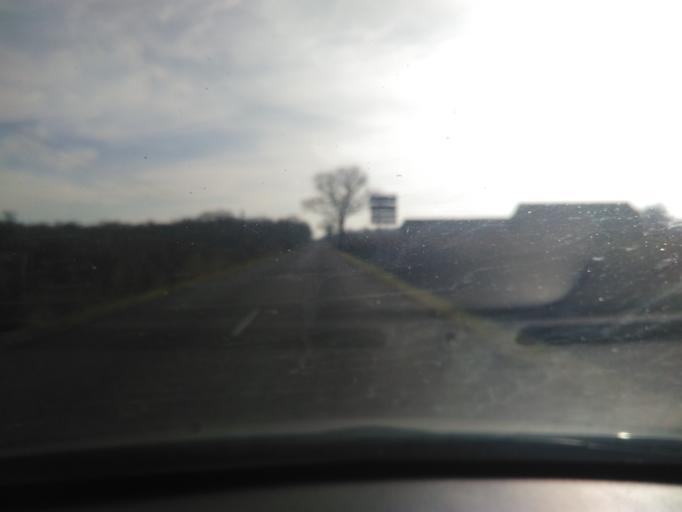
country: FR
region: Bourgogne
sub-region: Departement de la Nievre
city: Dornes
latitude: 46.7775
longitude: 3.2801
